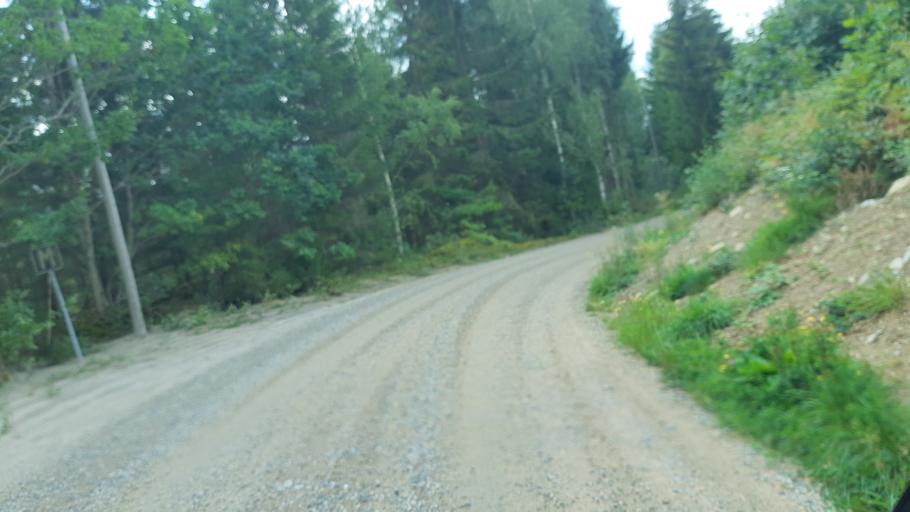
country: SE
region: Blekinge
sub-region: Ronneby Kommun
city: Brakne-Hoby
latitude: 56.4142
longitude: 15.1767
